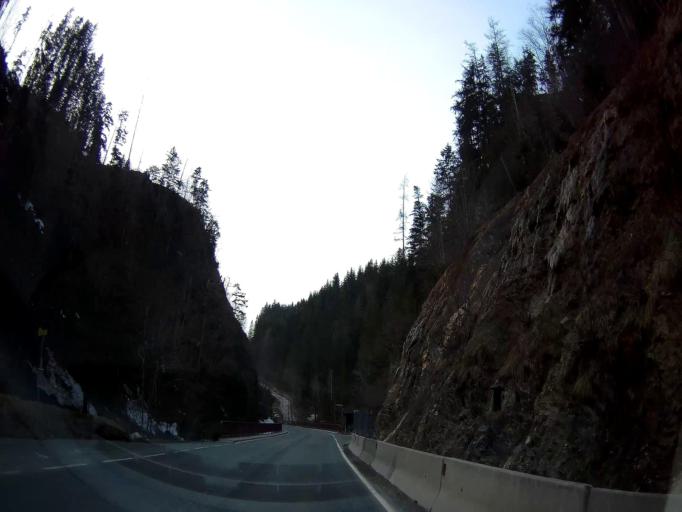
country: AT
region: Salzburg
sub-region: Politischer Bezirk Hallein
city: Abtenau
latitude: 47.5445
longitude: 13.4200
